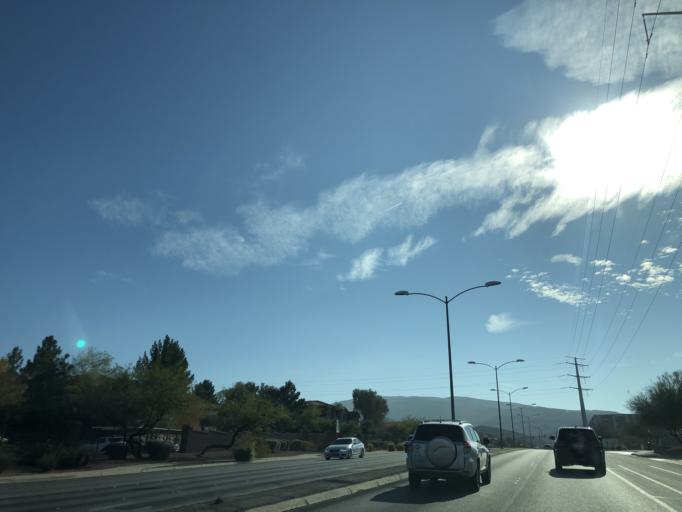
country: US
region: Nevada
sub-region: Clark County
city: Henderson
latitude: 36.0292
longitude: -115.0296
